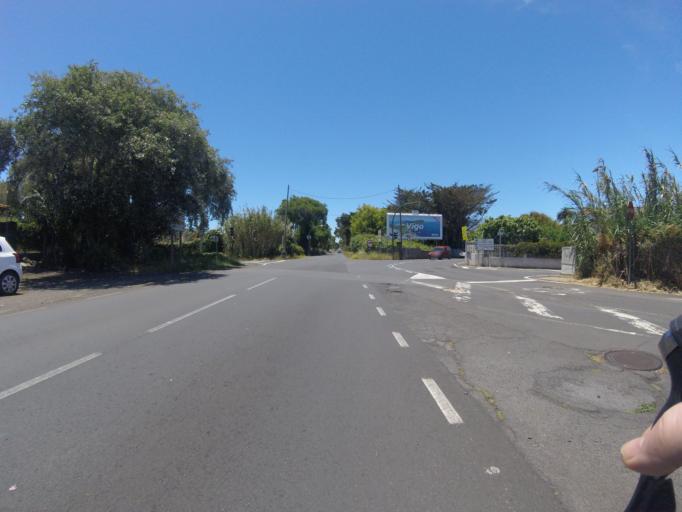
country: ES
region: Canary Islands
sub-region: Provincia de Santa Cruz de Tenerife
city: La Laguna
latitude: 28.5001
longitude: -16.3134
